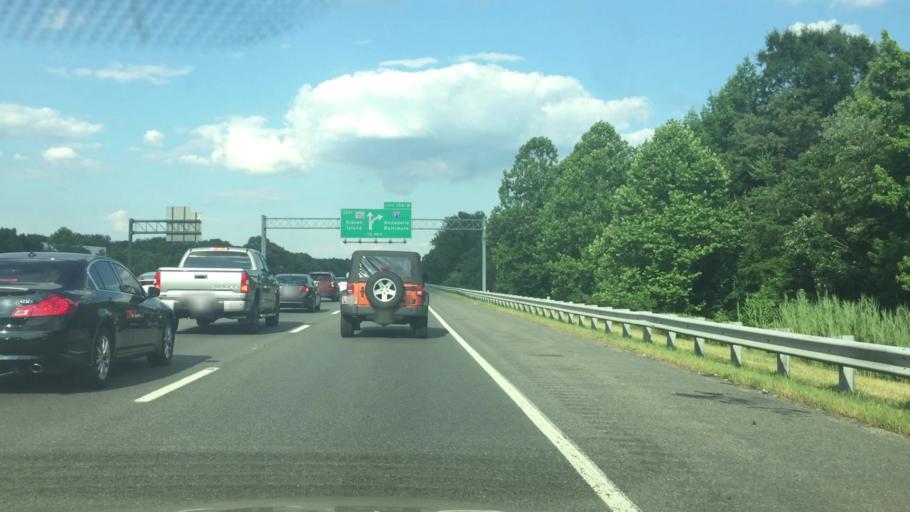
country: US
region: Maryland
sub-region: Anne Arundel County
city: Ferndale
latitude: 39.1564
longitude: -76.6637
